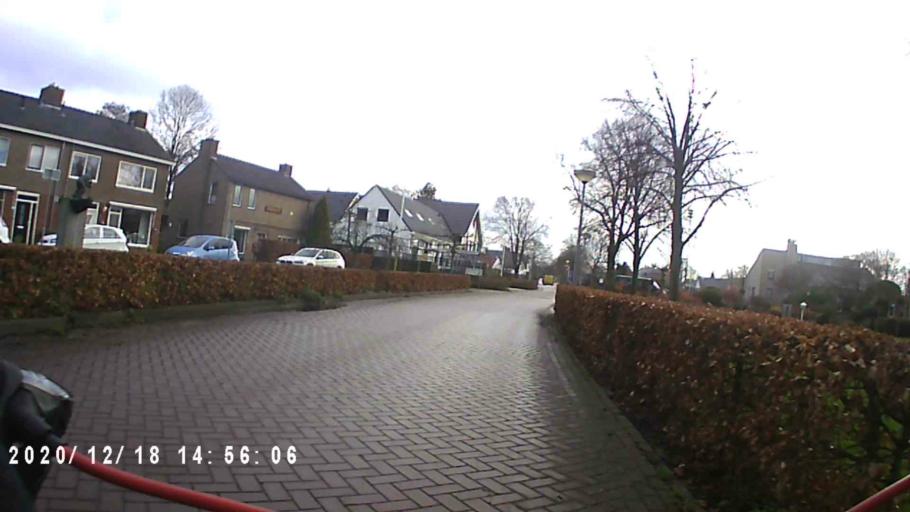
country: NL
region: Groningen
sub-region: Gemeente Haren
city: Haren
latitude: 53.1844
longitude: 6.6859
